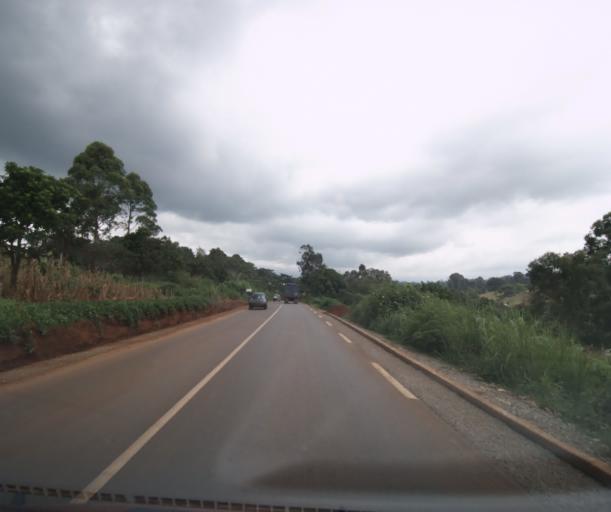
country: CM
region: West
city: Mbouda
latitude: 5.6627
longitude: 10.2248
